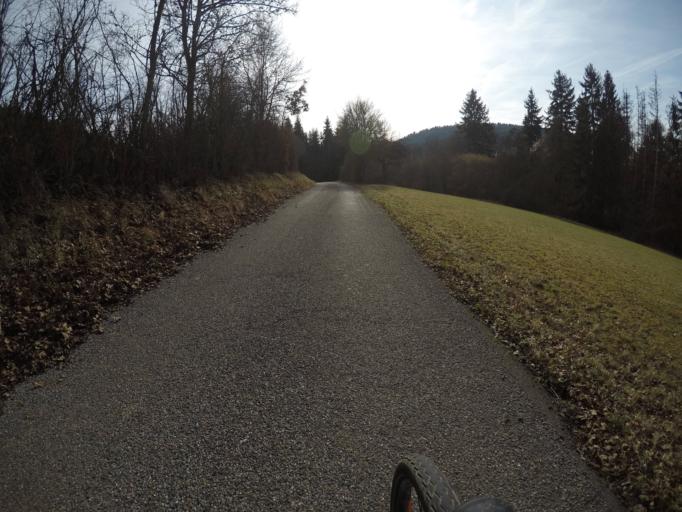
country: DE
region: Baden-Wuerttemberg
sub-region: Karlsruhe Region
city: Wildberg
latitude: 48.6349
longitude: 8.7666
